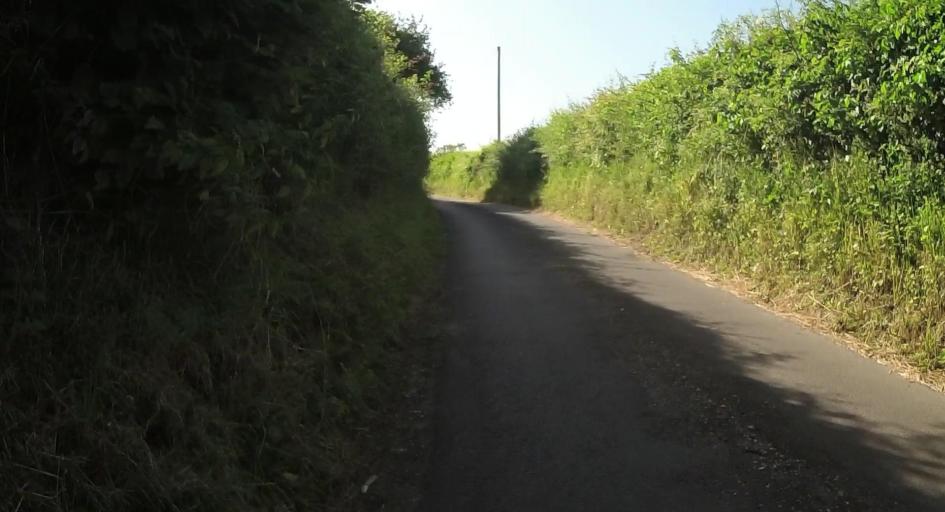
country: GB
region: England
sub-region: Hampshire
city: Long Sutton
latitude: 51.1827
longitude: -0.9283
